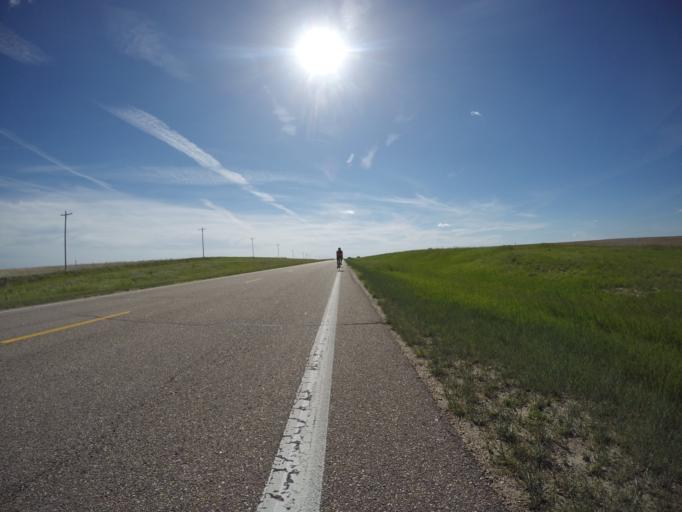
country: US
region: Kansas
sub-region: Cheyenne County
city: Saint Francis
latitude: 39.7567
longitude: -101.9784
